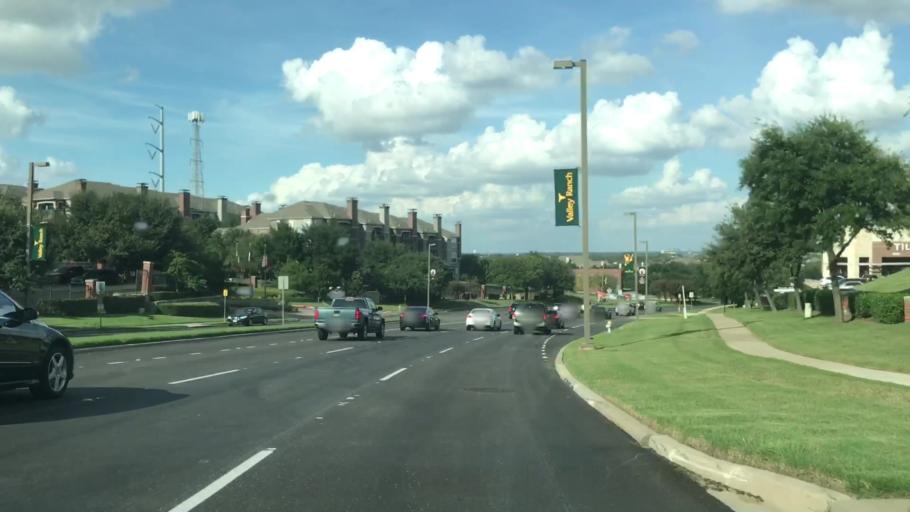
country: US
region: Texas
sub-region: Dallas County
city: Farmers Branch
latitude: 32.9212
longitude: -96.9583
